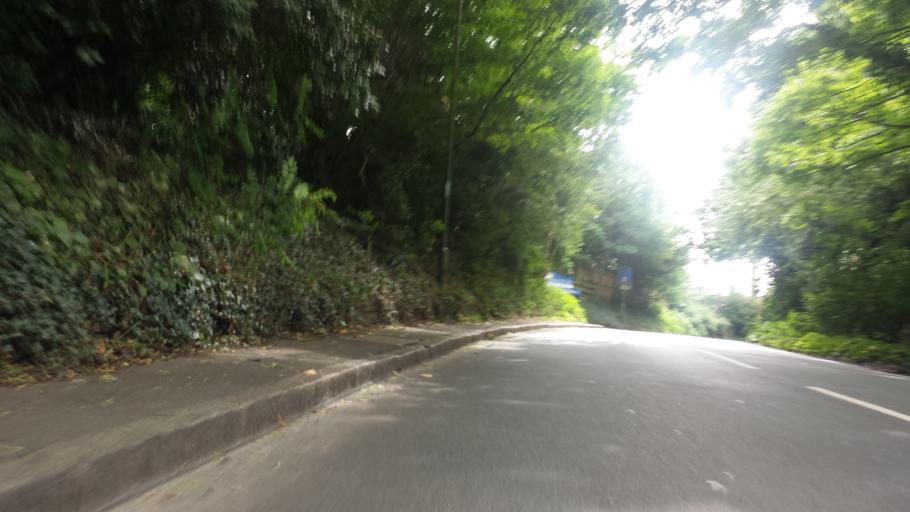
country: GB
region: England
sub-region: Greater London
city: Sidcup
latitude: 51.4041
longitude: 0.1198
